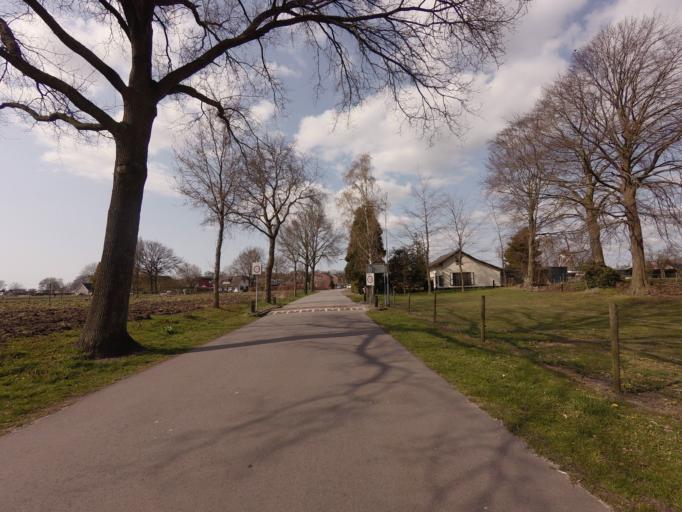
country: NL
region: Gelderland
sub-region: Gemeente Nunspeet
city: Nunspeet
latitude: 52.3599
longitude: 5.7339
